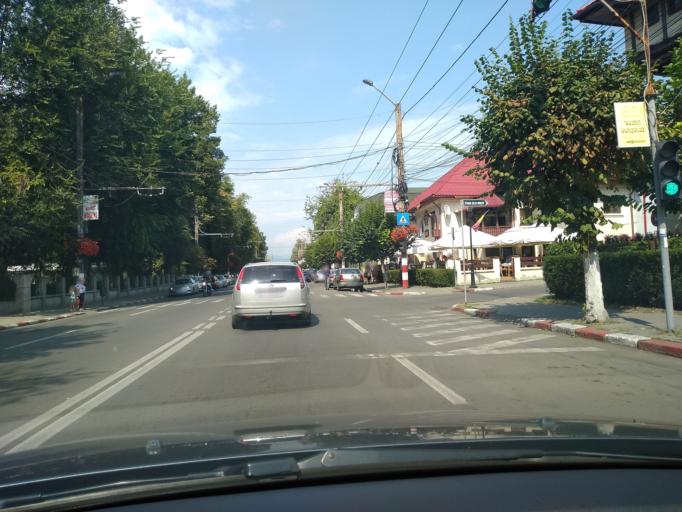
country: RO
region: Gorj
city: Targu Jiu
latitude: 45.0391
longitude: 23.2693
